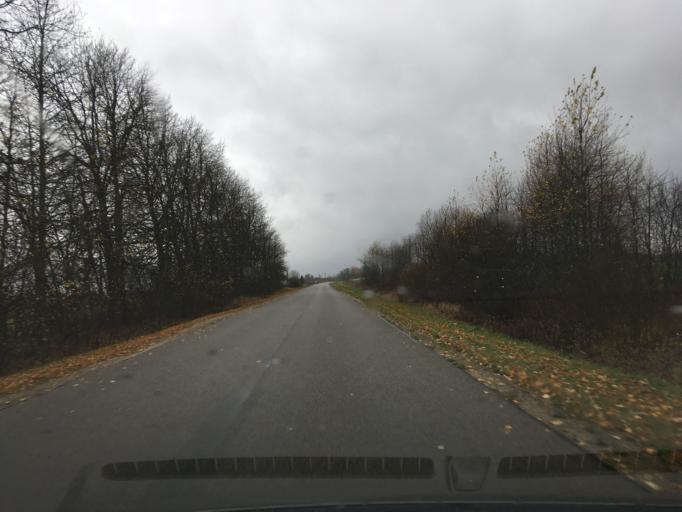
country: EE
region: Laeaene
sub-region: Lihula vald
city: Lihula
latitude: 58.6983
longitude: 23.8536
